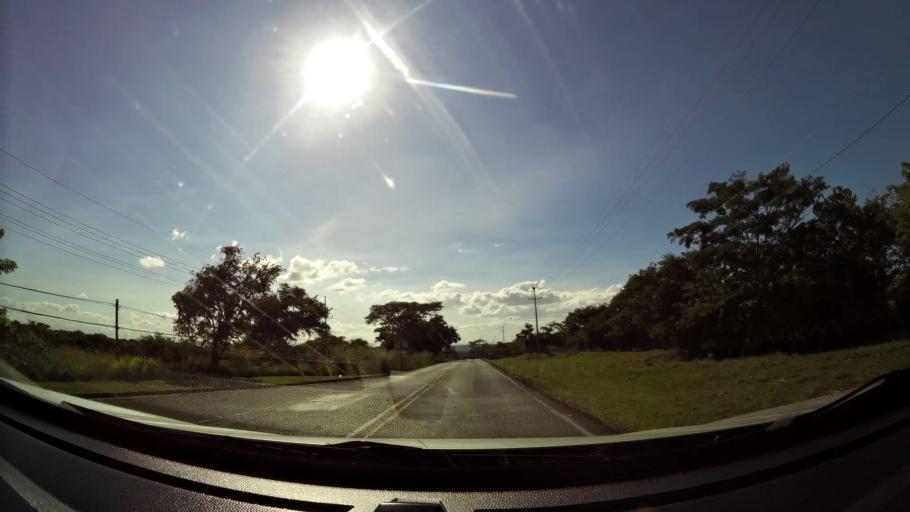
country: CR
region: Guanacaste
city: Sardinal
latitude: 10.5839
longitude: -85.5627
